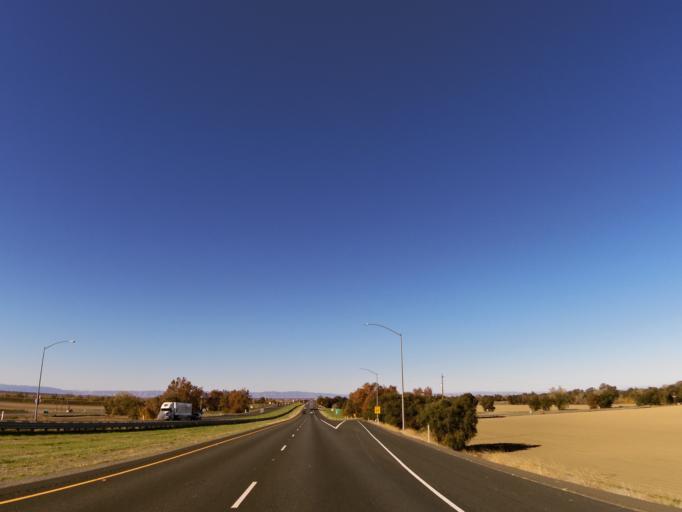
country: US
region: California
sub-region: Yolo County
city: West Sacramento
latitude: 38.6735
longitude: -121.6332
